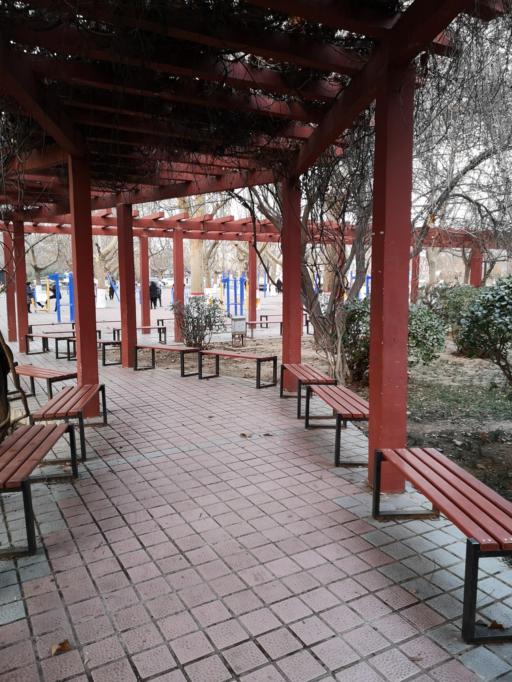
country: CN
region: Henan Sheng
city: Zhongyuanlu
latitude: 35.7747
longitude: 115.0775
